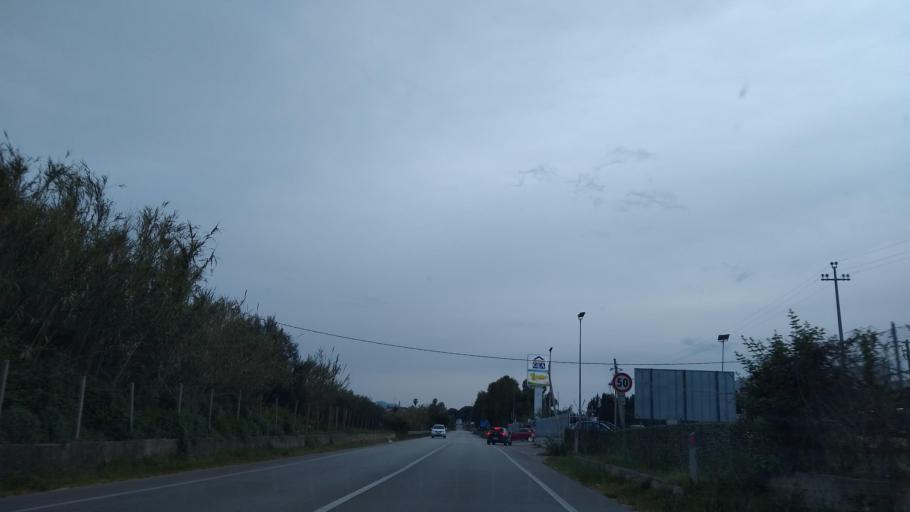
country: IT
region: Sicily
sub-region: Palermo
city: Partinico
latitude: 38.0309
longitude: 13.0945
